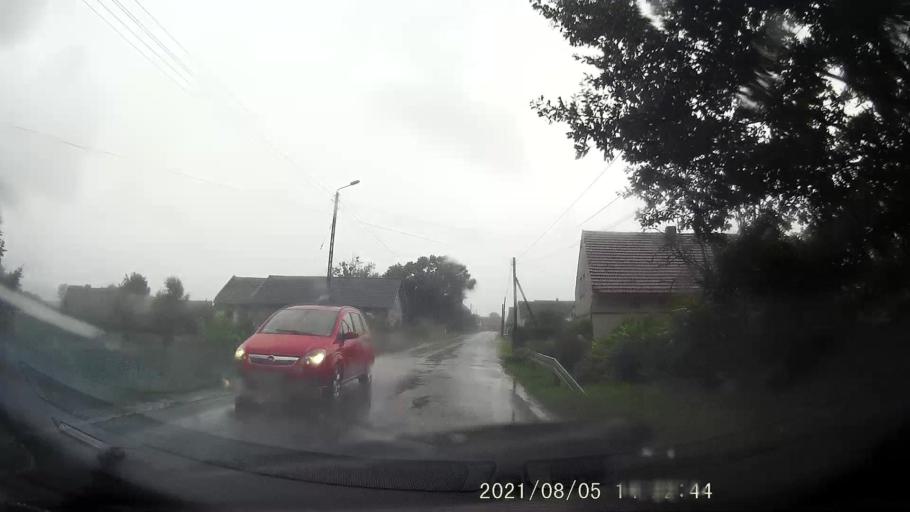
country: PL
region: Opole Voivodeship
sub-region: Powiat nyski
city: Korfantow
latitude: 50.4786
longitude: 17.6540
